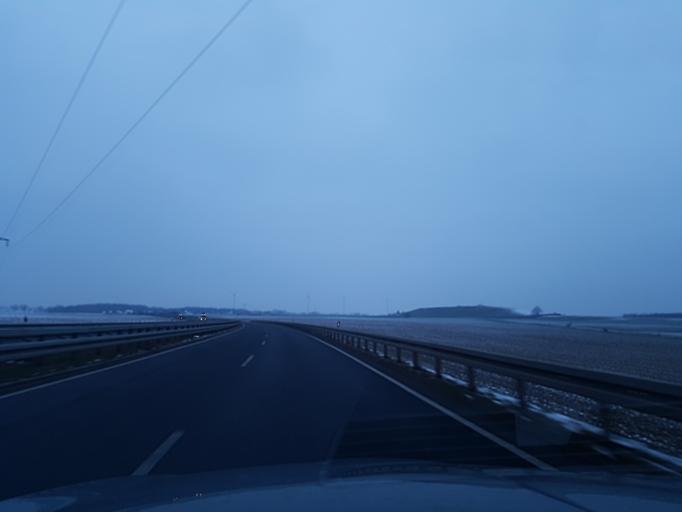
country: DE
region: Saxony
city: Riesa
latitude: 51.2876
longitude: 13.2663
